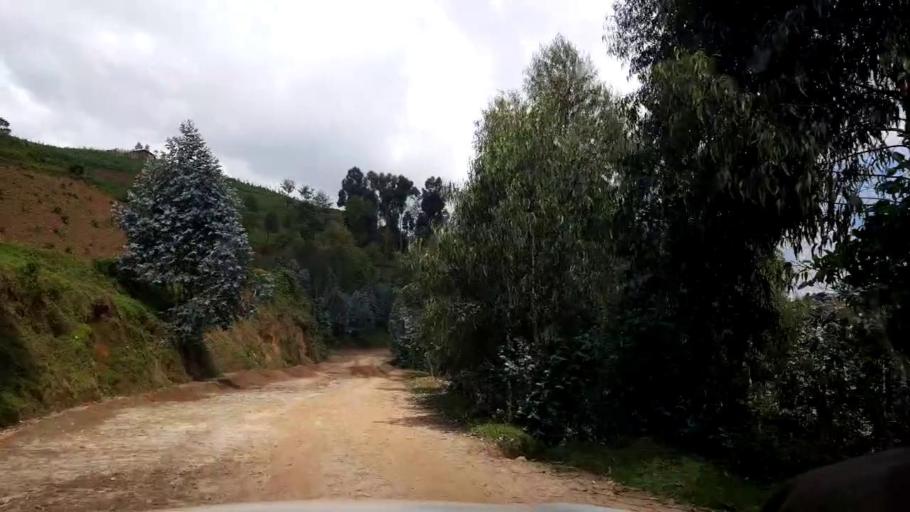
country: RW
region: Western Province
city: Kibuye
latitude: -1.8923
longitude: 29.4576
